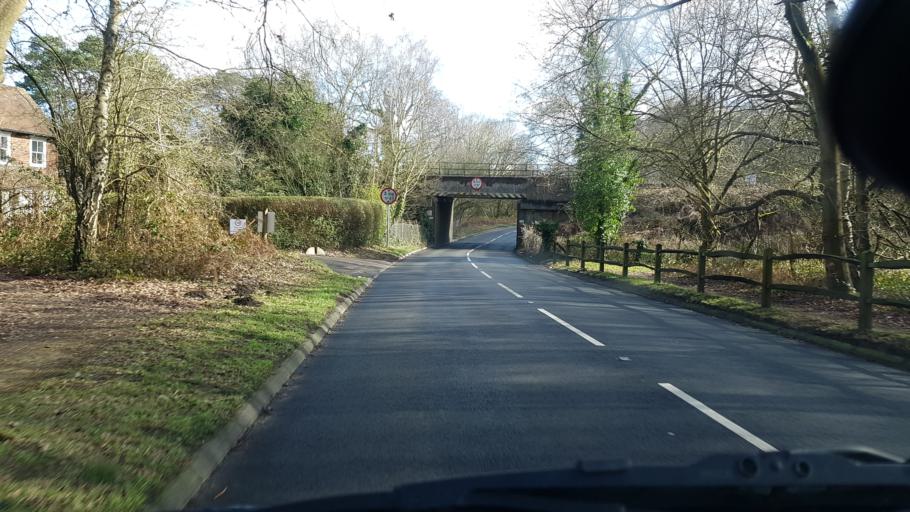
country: GB
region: England
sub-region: Surrey
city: Guildford
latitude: 51.2677
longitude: -0.5850
